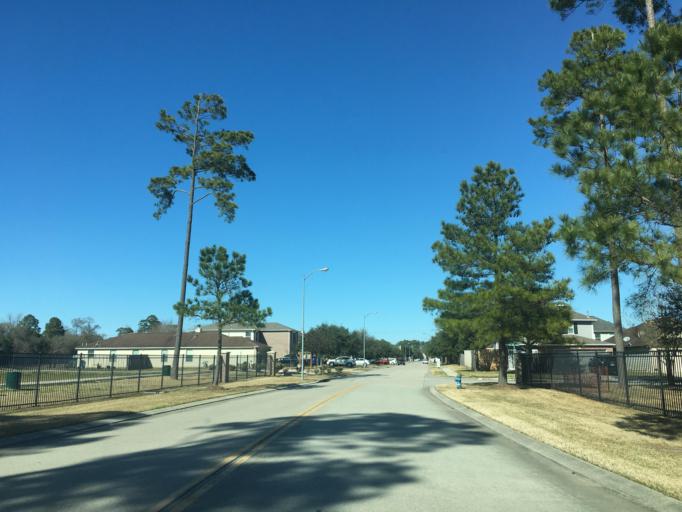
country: US
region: Texas
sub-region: Harris County
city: Spring
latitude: 30.0836
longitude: -95.4644
